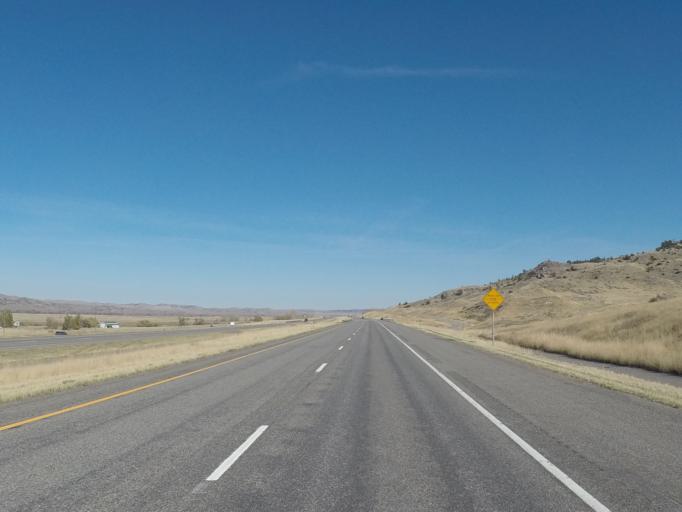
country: US
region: Montana
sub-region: Sweet Grass County
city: Big Timber
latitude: 45.7900
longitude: -110.0448
